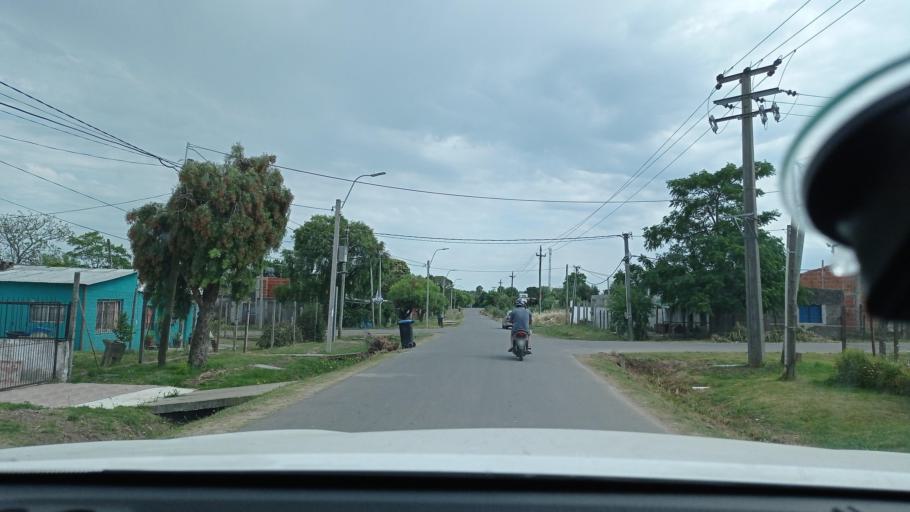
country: UY
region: Canelones
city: Pando
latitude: -34.7167
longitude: -55.9695
